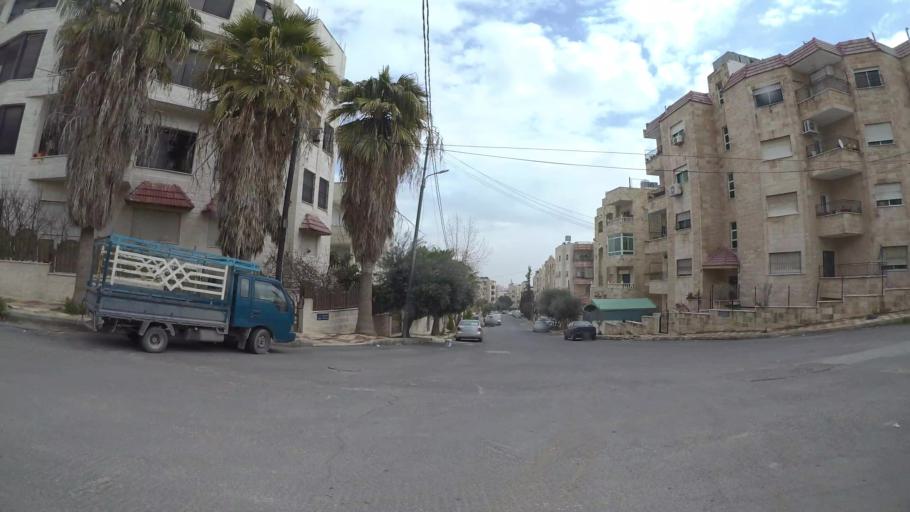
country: JO
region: Amman
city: Amman
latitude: 31.9908
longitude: 35.9240
